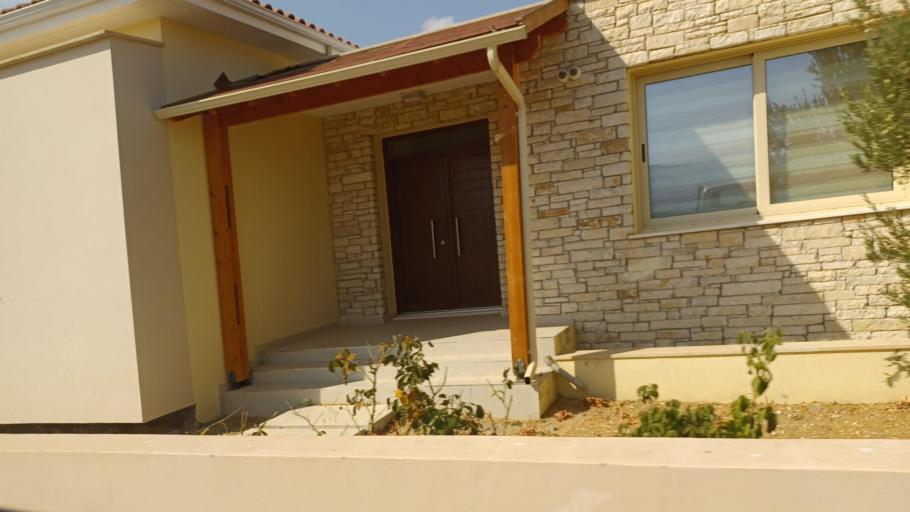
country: CY
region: Pafos
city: Polis
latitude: 34.9925
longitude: 32.4330
